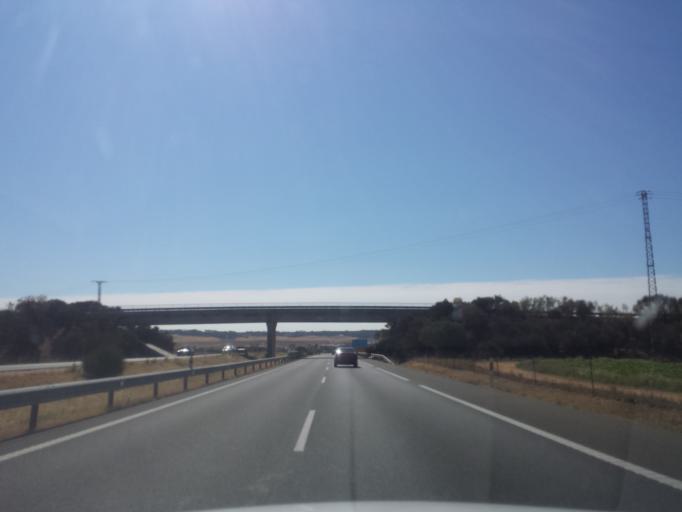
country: ES
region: Castille and Leon
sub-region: Provincia de Valladolid
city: Marzales
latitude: 41.6048
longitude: -5.1367
